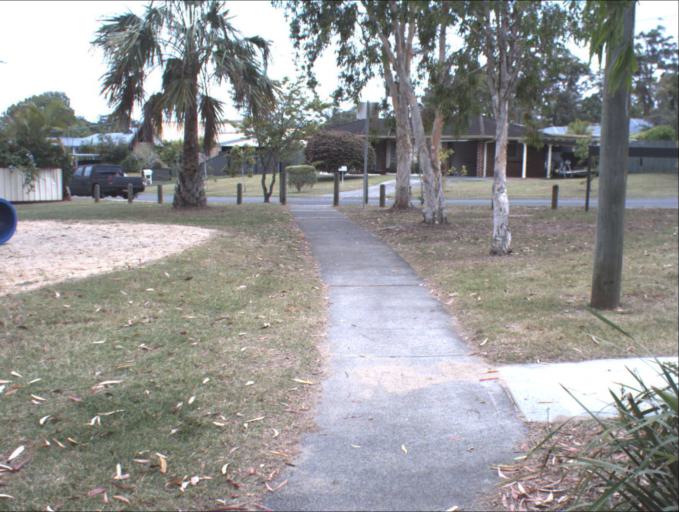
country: AU
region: Queensland
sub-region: Logan
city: Slacks Creek
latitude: -27.6337
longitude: 153.1437
